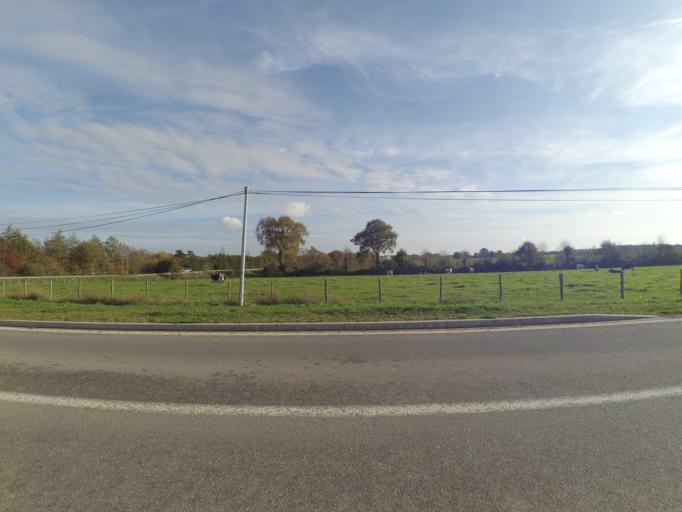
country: FR
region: Pays de la Loire
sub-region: Departement de la Vendee
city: Saint-Hilaire-de-Loulay
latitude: 47.0171
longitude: -1.3439
